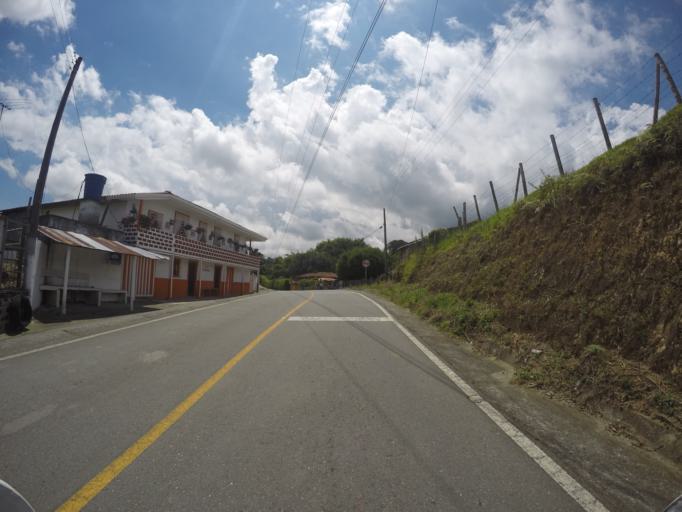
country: CO
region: Quindio
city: Filandia
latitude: 4.6429
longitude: -75.6836
